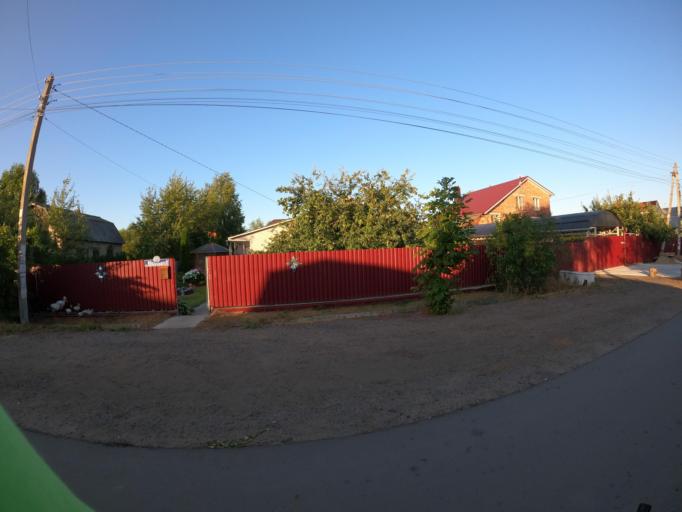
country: RU
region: Moskovskaya
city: Beloozerskiy
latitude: 55.4662
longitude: 38.4209
